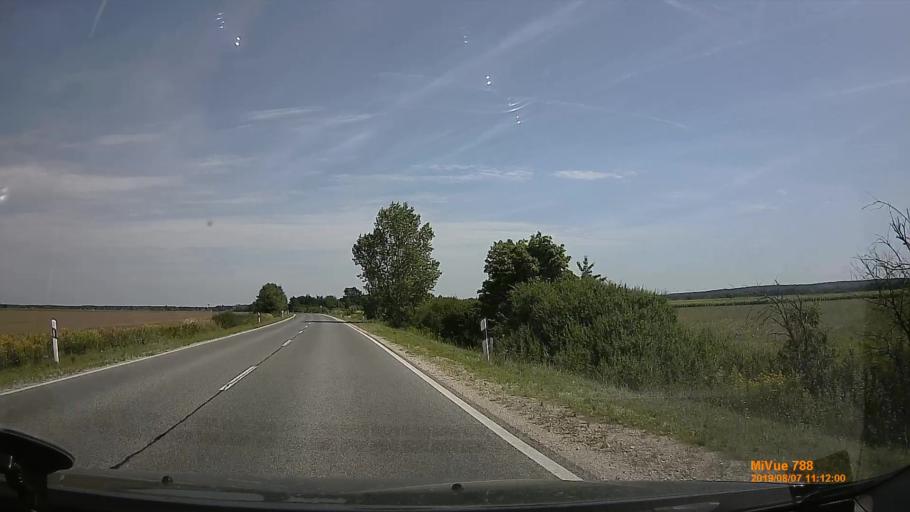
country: HU
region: Zala
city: Lenti
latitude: 46.6852
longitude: 16.5337
